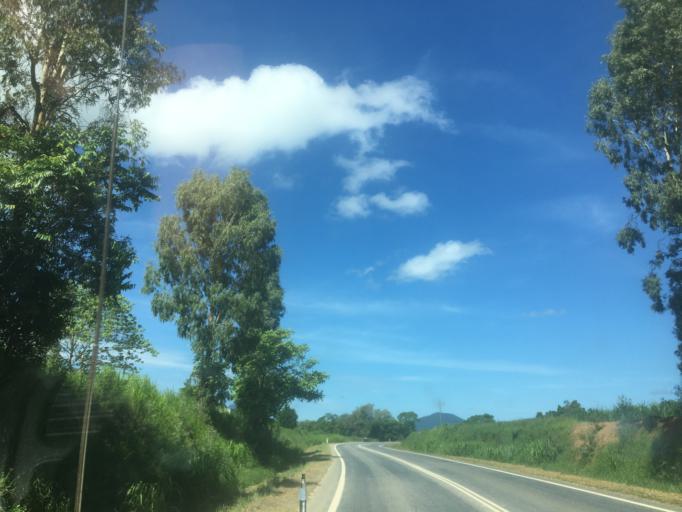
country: AU
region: Queensland
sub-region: Cairns
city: Woree
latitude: -17.0681
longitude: 145.7472
